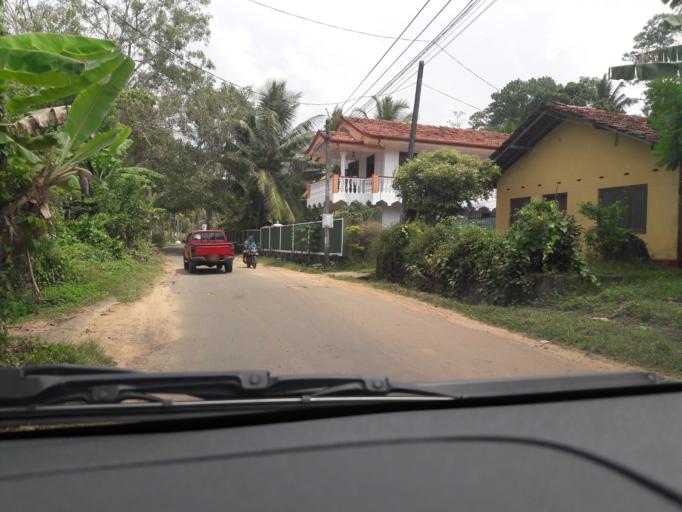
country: LK
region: Southern
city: Hikkaduwa
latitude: 6.1031
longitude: 80.1534
